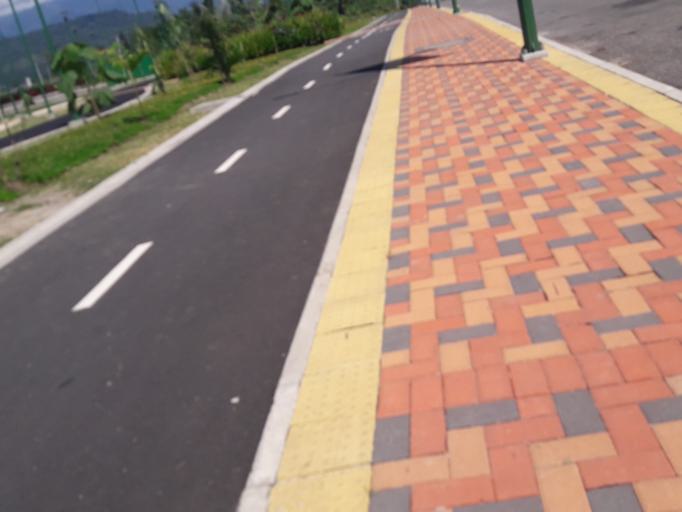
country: EC
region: Napo
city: Tena
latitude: -0.9854
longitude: -77.8227
